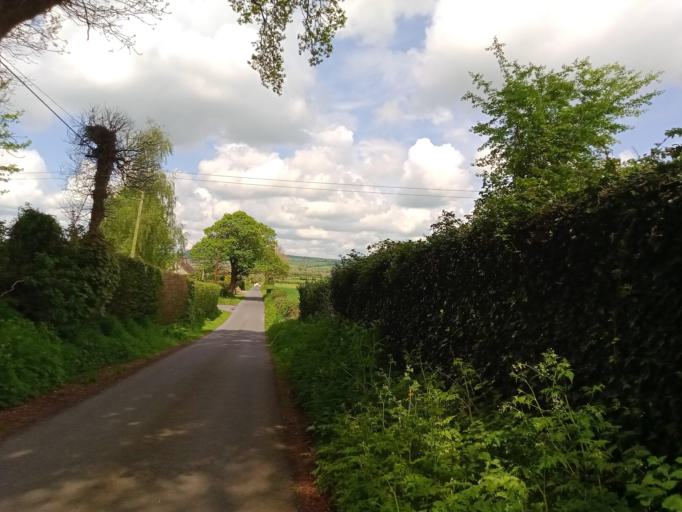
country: IE
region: Leinster
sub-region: Kilkenny
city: Ballyragget
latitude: 52.7299
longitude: -7.4178
